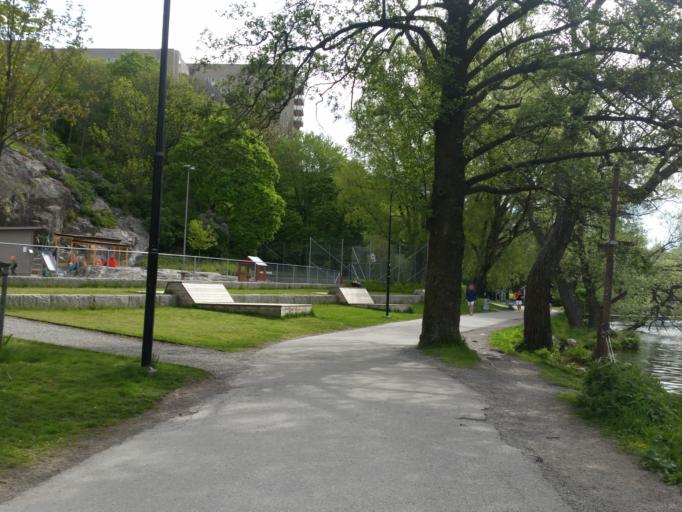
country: SE
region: Stockholm
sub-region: Stockholms Kommun
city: Arsta
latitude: 59.3090
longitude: 18.0483
